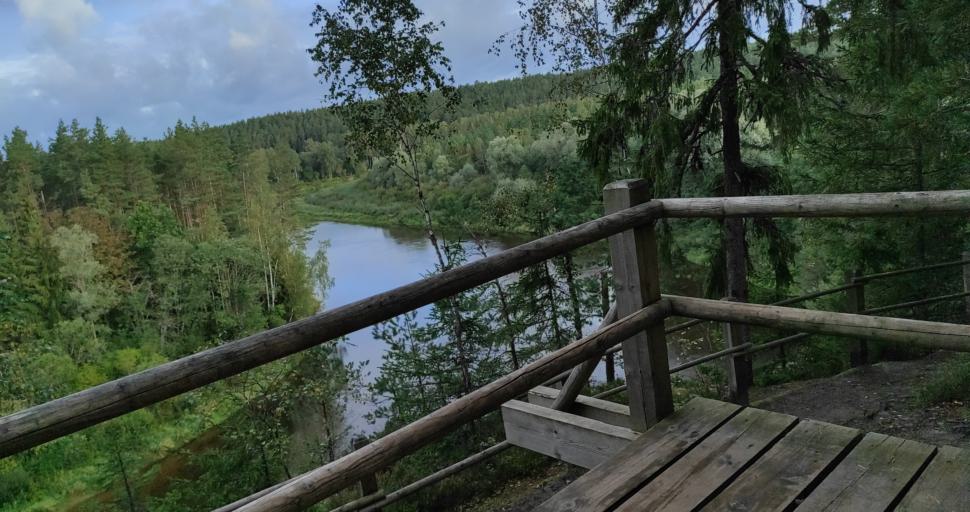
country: LV
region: Cesu Rajons
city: Cesis
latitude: 57.3607
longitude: 25.2607
